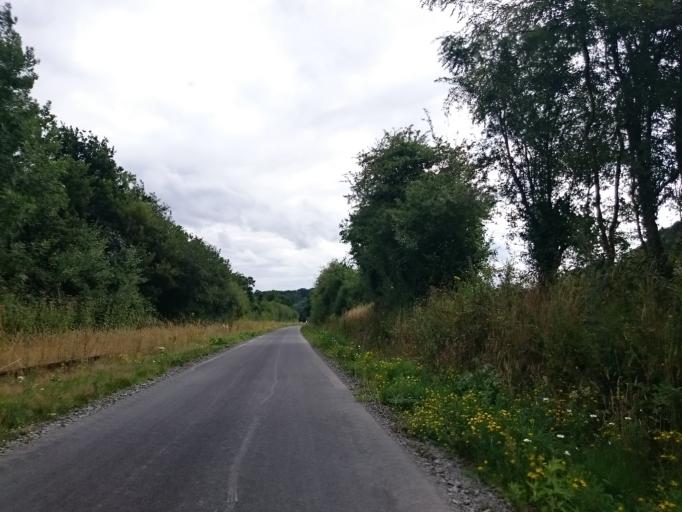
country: FR
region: Lower Normandy
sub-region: Departement du Calvados
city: Thury-Harcourt
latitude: 49.0162
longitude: -0.4686
